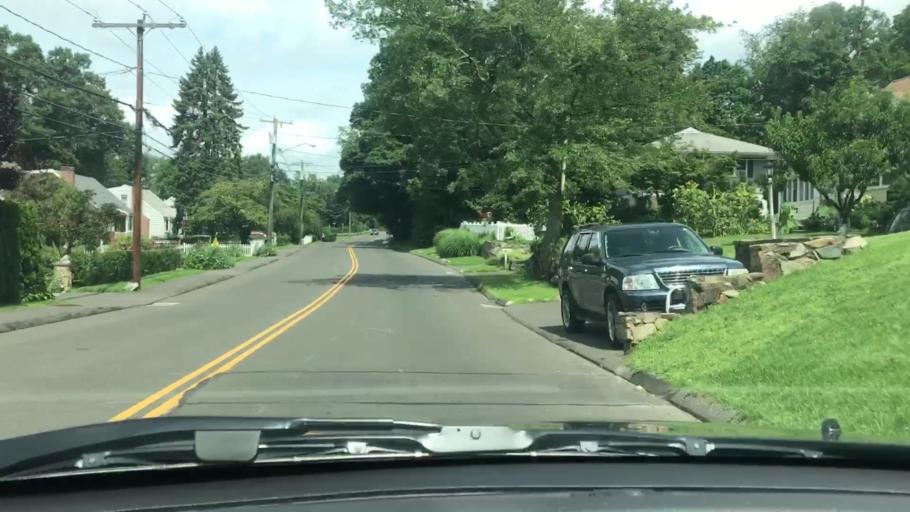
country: US
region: Connecticut
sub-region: Fairfield County
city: Norwalk
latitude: 41.0987
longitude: -73.4360
